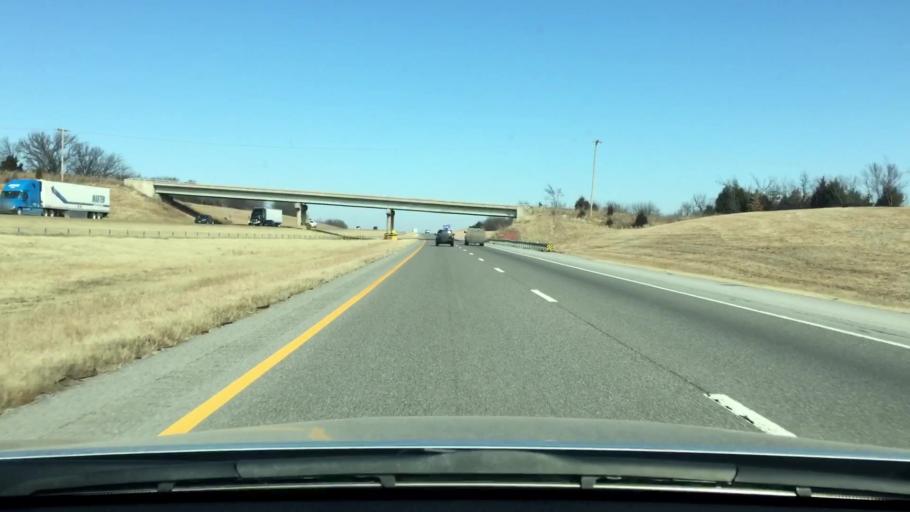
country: US
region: Oklahoma
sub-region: McClain County
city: Purcell
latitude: 34.9557
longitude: -97.3687
